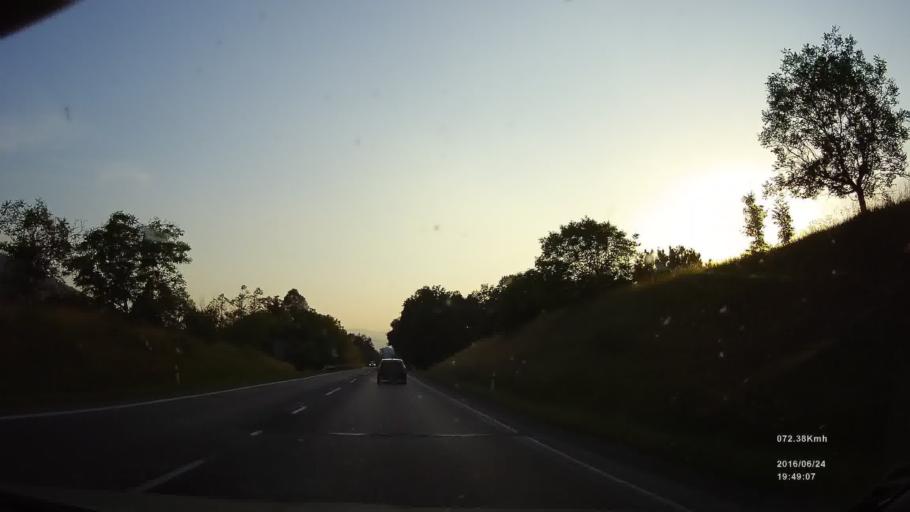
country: SK
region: Banskobystricky
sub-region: Okres Banska Bystrica
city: Banska Bystrica
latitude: 48.7431
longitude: 19.2146
